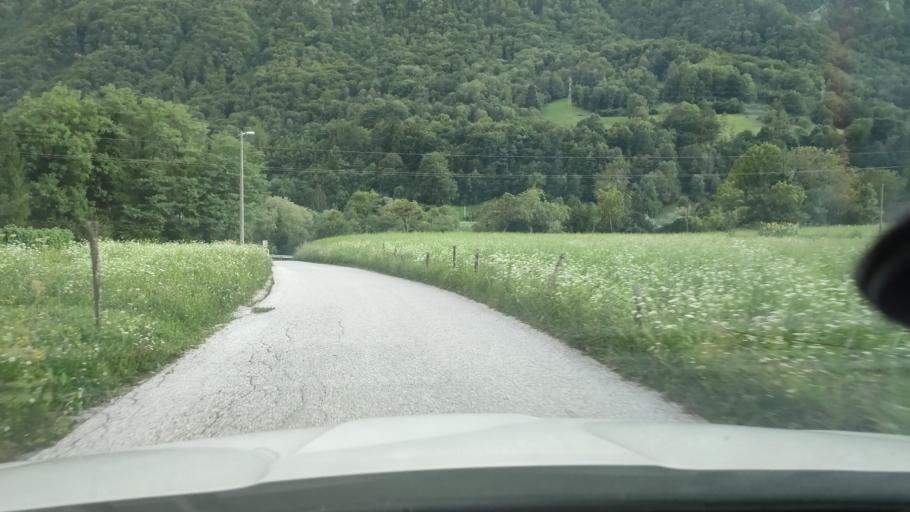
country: IT
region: Friuli Venezia Giulia
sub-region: Provincia di Udine
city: Cras
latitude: 46.2121
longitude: 13.6366
